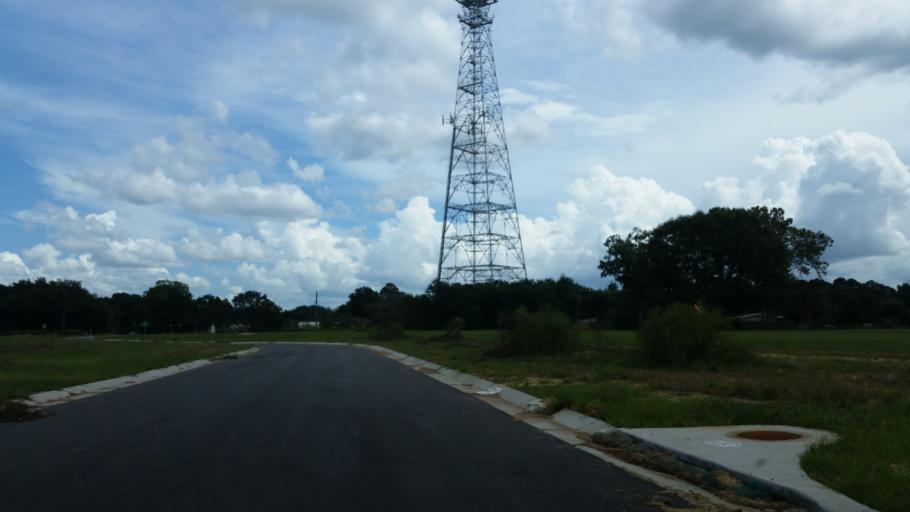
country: US
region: Florida
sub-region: Escambia County
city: Cantonment
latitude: 30.5367
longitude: -87.4085
